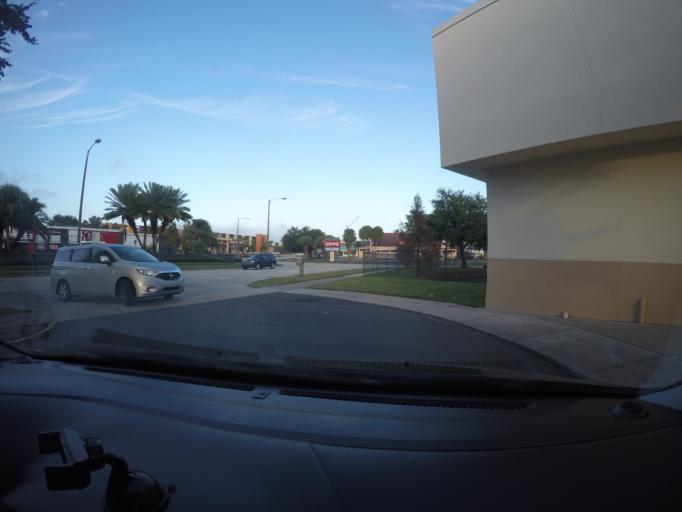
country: US
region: Florida
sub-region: Orange County
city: Tangelo Park
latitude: 28.4626
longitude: -81.4651
